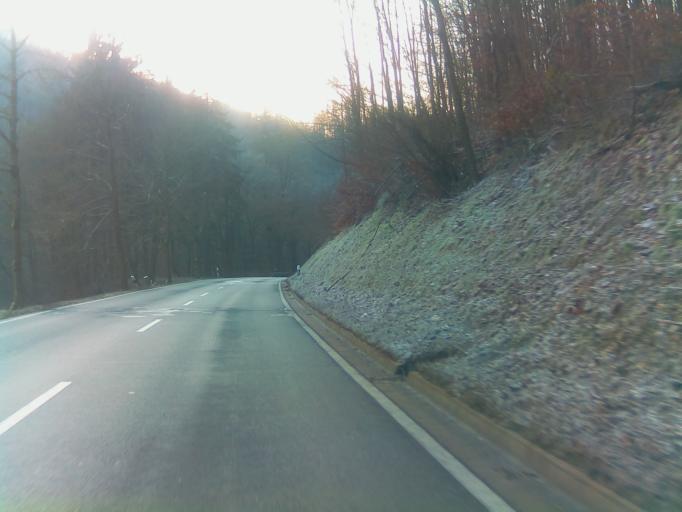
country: DE
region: Thuringia
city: Judenbach
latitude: 50.3710
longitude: 11.2159
